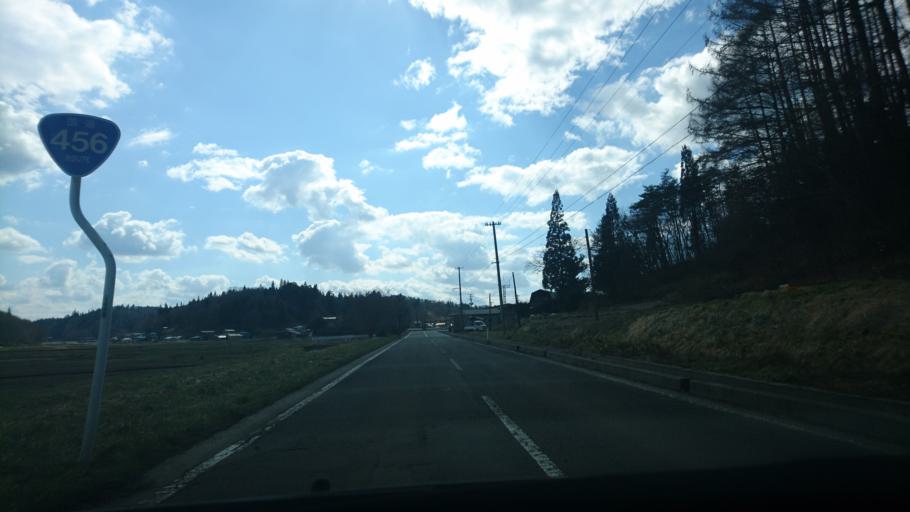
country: JP
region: Iwate
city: Kitakami
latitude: 39.3240
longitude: 141.2227
